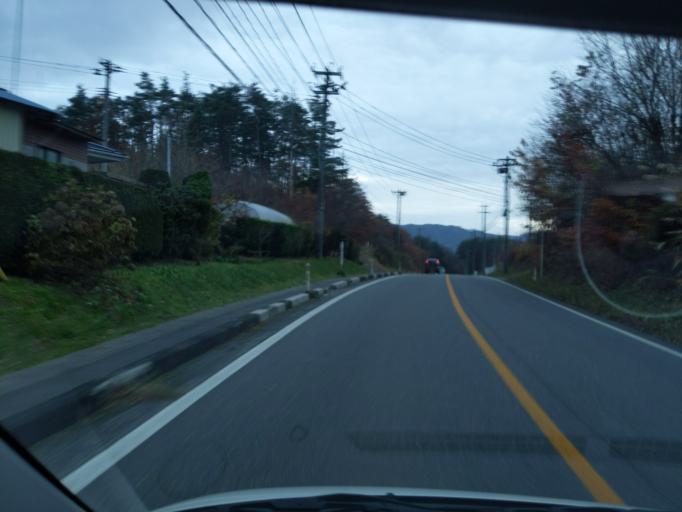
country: JP
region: Iwate
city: Ichinoseki
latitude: 39.0044
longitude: 141.3260
